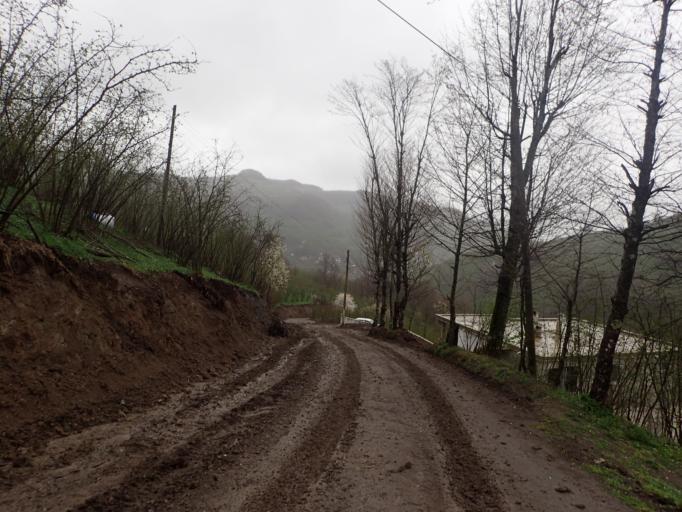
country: TR
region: Ordu
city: Korgan
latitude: 40.8042
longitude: 37.2876
